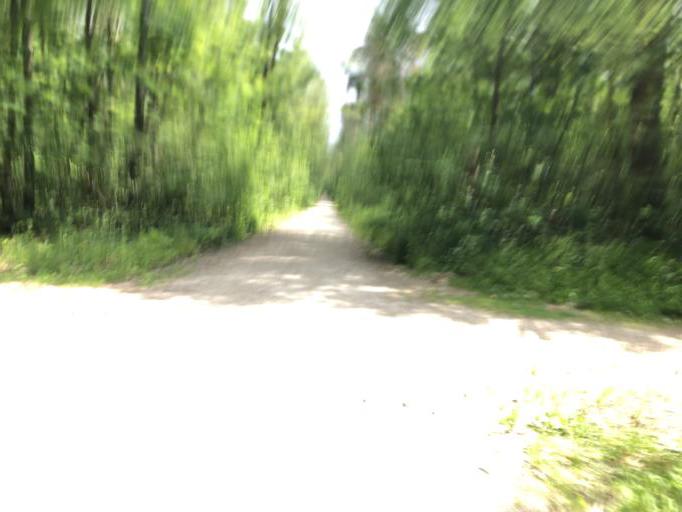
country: DE
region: Bavaria
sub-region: Regierungsbezirk Mittelfranken
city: Mohrendorf
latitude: 49.6137
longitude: 10.9606
